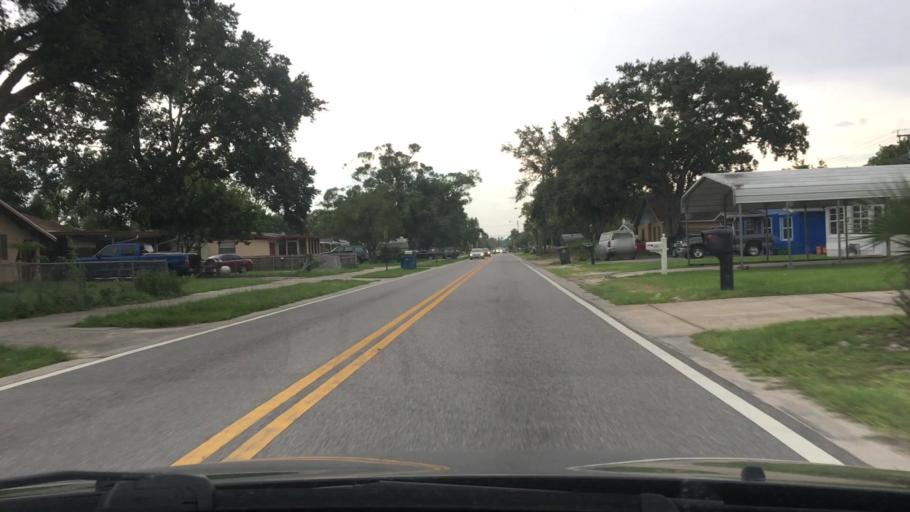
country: US
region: Florida
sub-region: Volusia County
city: Holly Hill
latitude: 29.2284
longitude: -81.0623
